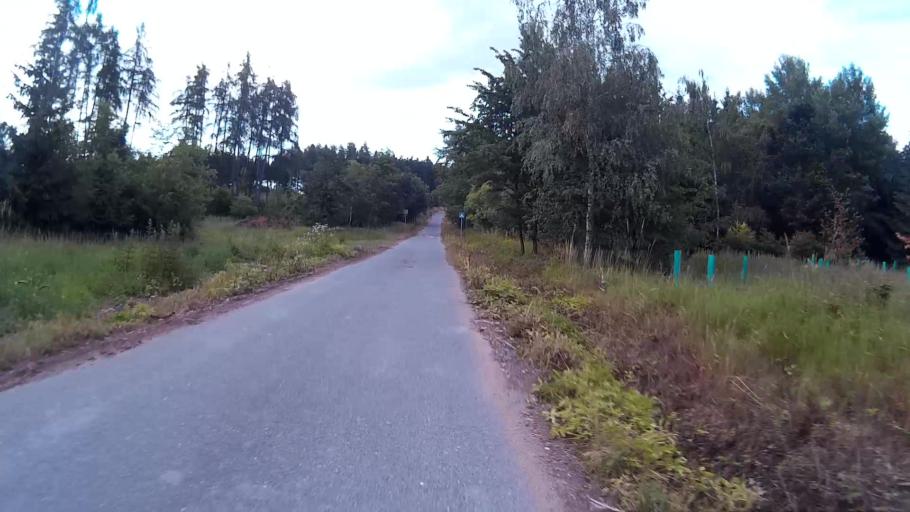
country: CZ
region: South Moravian
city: Veverska Bityska
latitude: 49.2272
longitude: 16.4574
